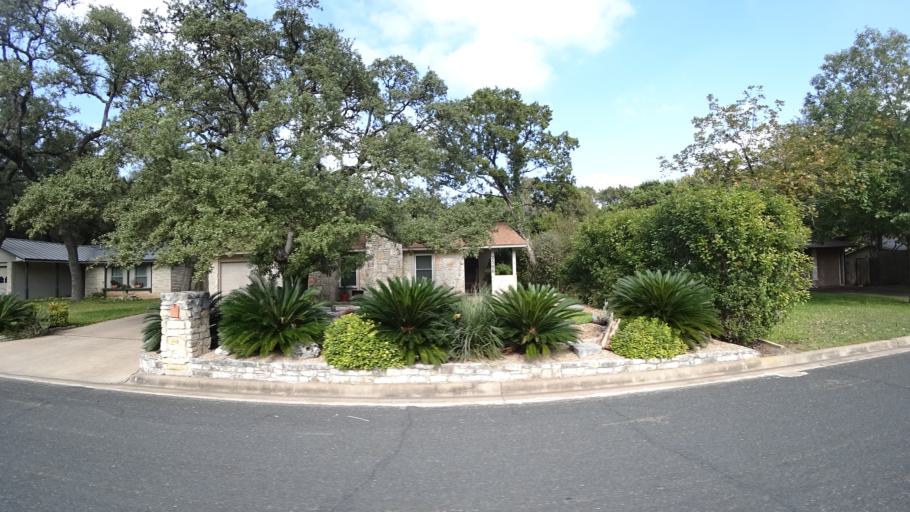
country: US
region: Texas
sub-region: Travis County
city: Shady Hollow
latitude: 30.2000
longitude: -97.8158
